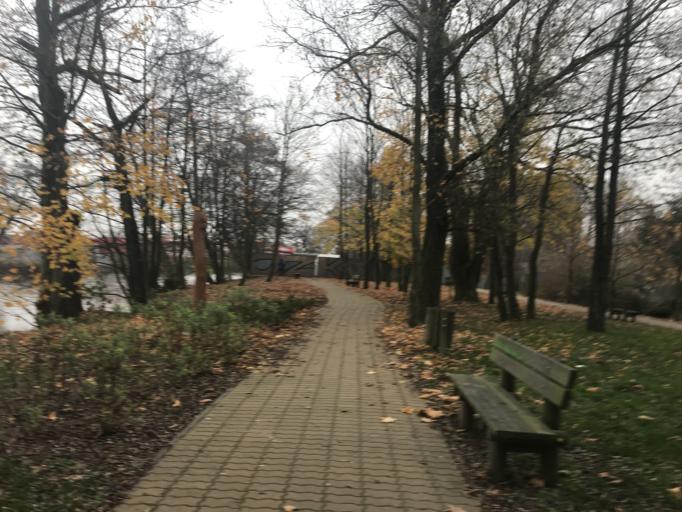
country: PL
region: West Pomeranian Voivodeship
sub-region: Powiat slawienski
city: Darlowo
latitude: 54.4160
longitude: 16.4142
